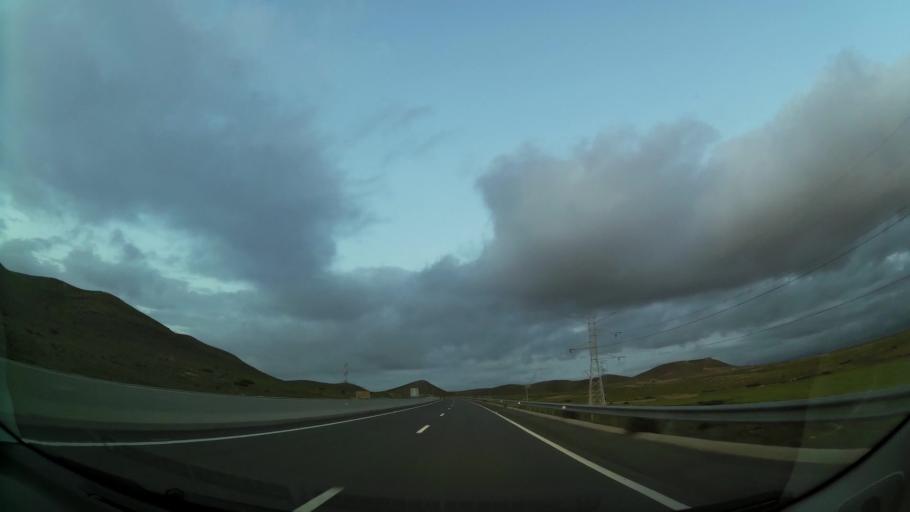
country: MA
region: Oriental
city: El Aioun
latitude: 34.6143
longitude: -2.4268
